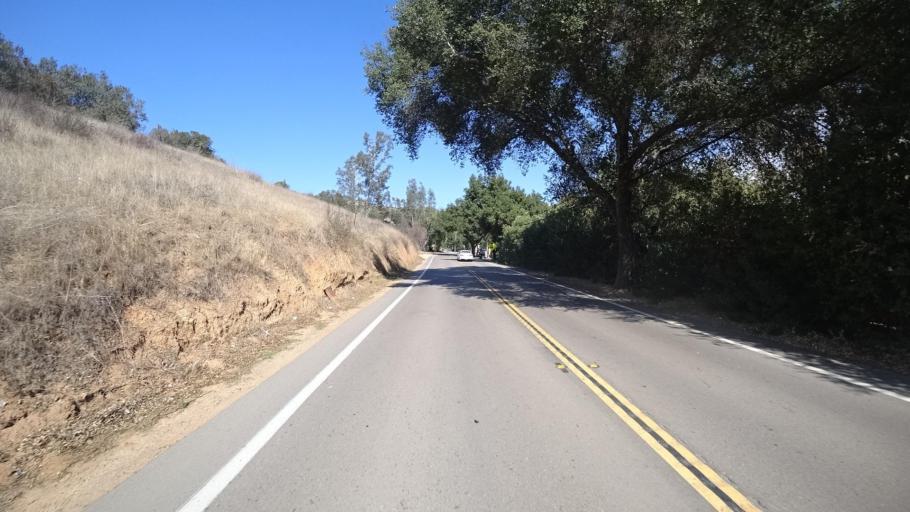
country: US
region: California
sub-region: San Diego County
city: Crest
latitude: 32.8004
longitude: -116.8452
